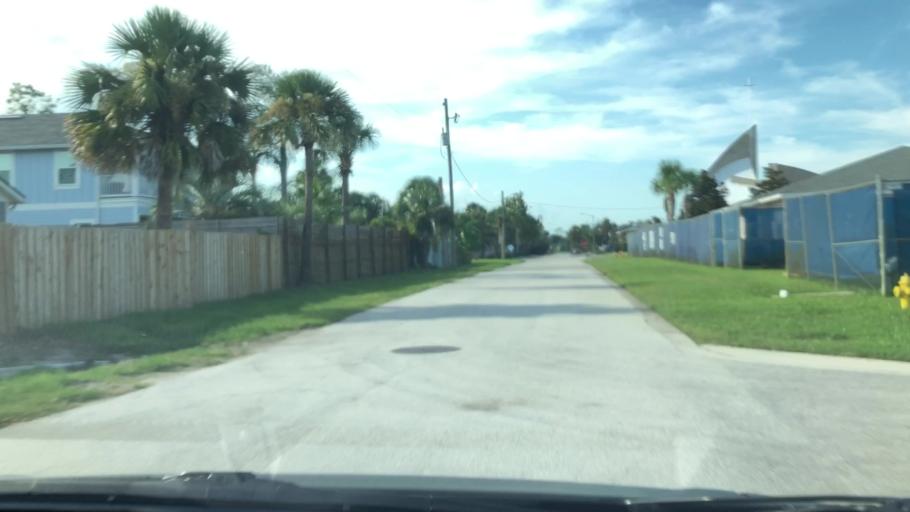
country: US
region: Florida
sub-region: Duval County
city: Jacksonville Beach
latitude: 30.2981
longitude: -81.3961
